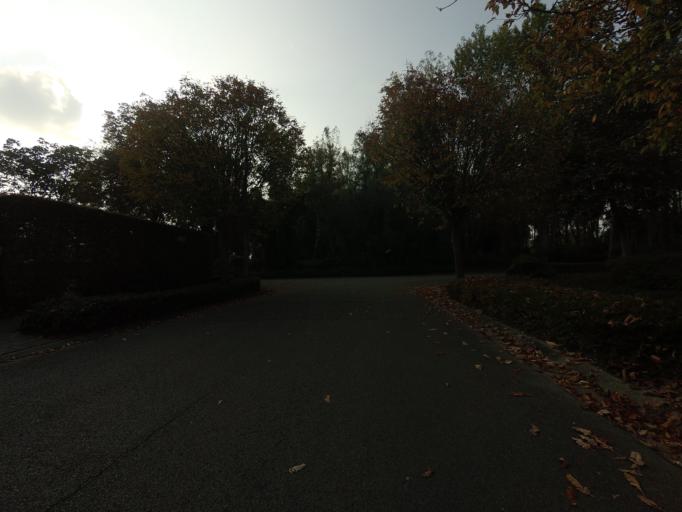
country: BE
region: Flanders
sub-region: Provincie Antwerpen
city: Willebroek
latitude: 51.0470
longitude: 4.3526
